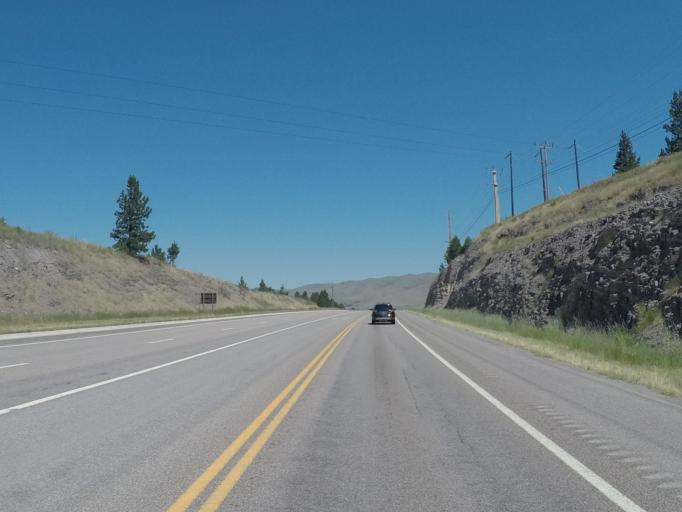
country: US
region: Montana
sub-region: Missoula County
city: Frenchtown
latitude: 47.1804
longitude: -114.1007
